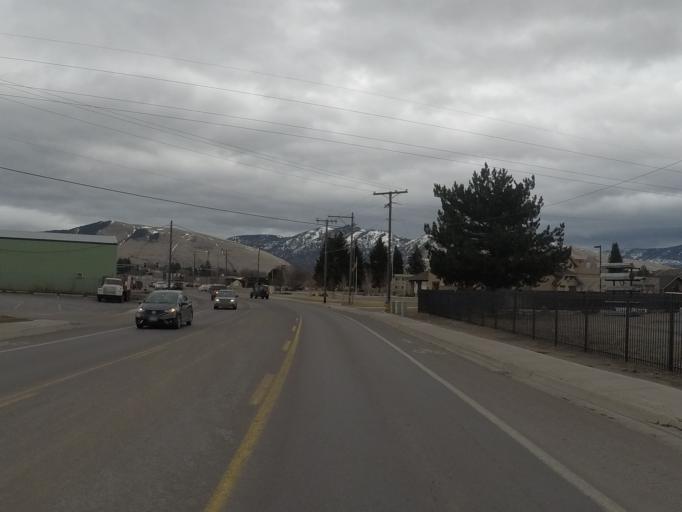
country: US
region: Montana
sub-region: Missoula County
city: Orchard Homes
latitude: 46.8808
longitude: -114.0245
